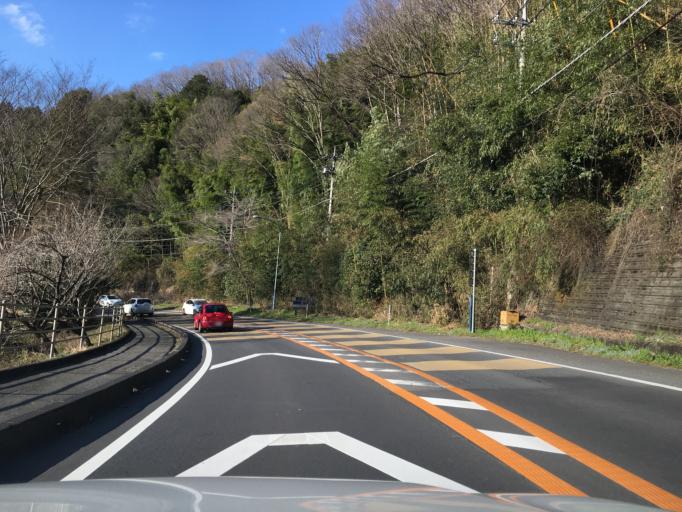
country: JP
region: Ibaraki
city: Daigo
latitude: 36.7602
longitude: 140.3817
